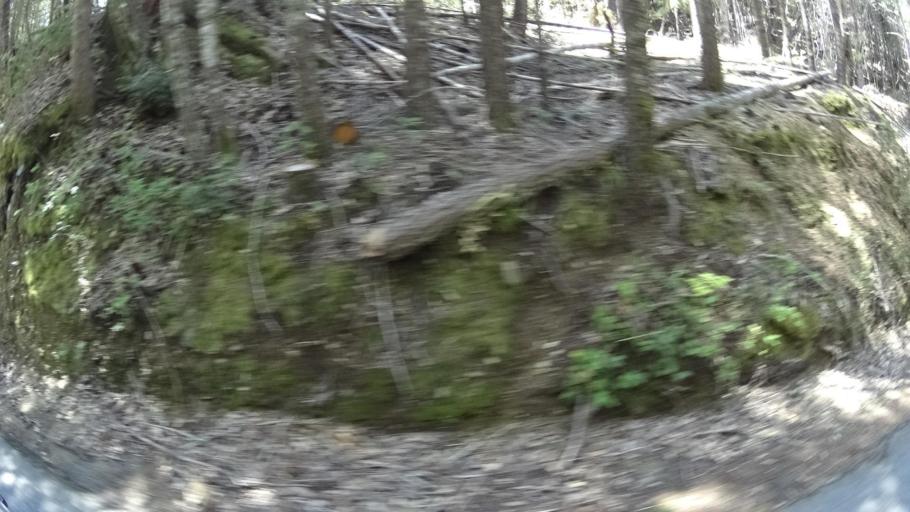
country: US
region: California
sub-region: Humboldt County
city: Rio Dell
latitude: 40.3107
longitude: -124.0615
